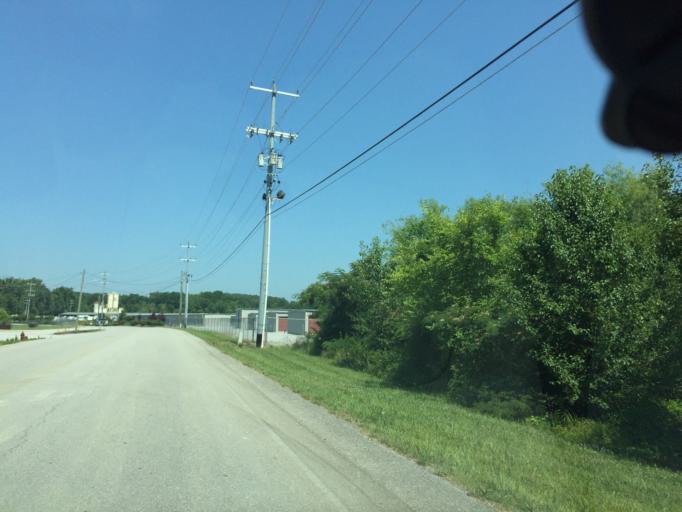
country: US
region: Tennessee
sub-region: Hamilton County
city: Collegedale
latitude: 35.0773
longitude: -85.0617
